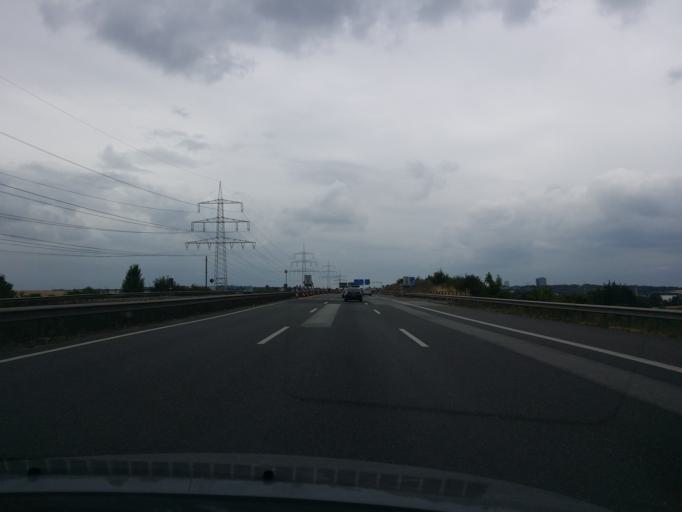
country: DE
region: Rheinland-Pfalz
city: Mainz
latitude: 49.9668
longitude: 8.2521
